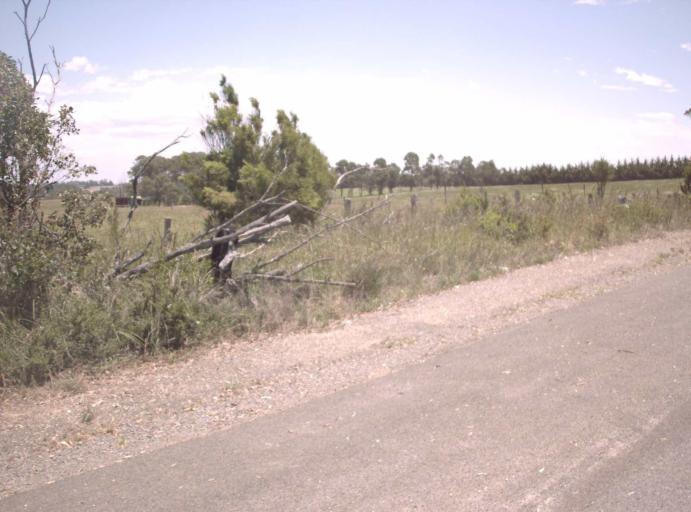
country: AU
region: Victoria
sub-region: East Gippsland
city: Lakes Entrance
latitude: -37.8396
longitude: 148.0343
